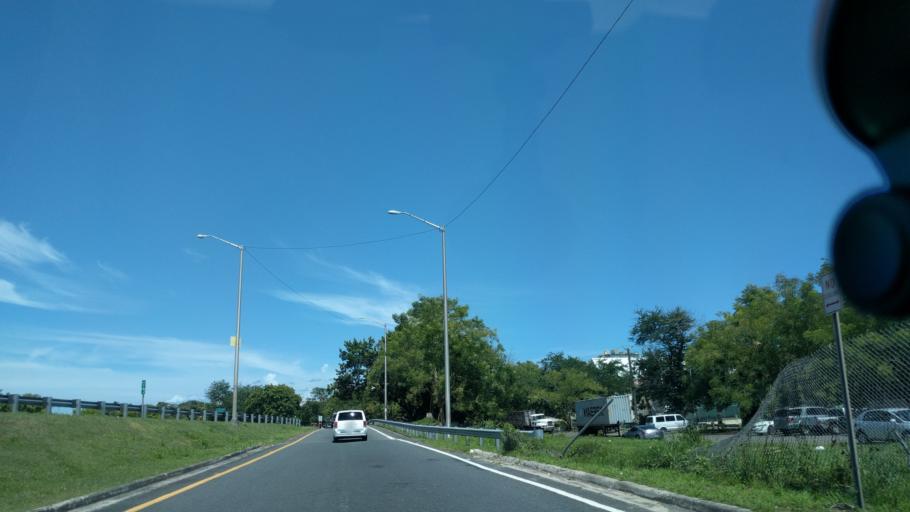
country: PR
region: San Juan
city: San Juan
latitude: 18.4381
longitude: -66.0621
